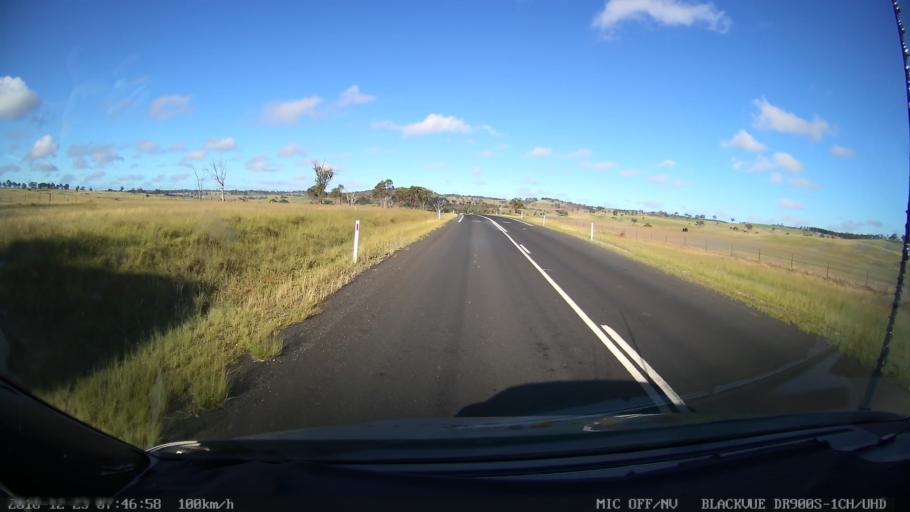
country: AU
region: New South Wales
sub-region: Armidale Dumaresq
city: Enmore
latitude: -30.5255
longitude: 151.9093
